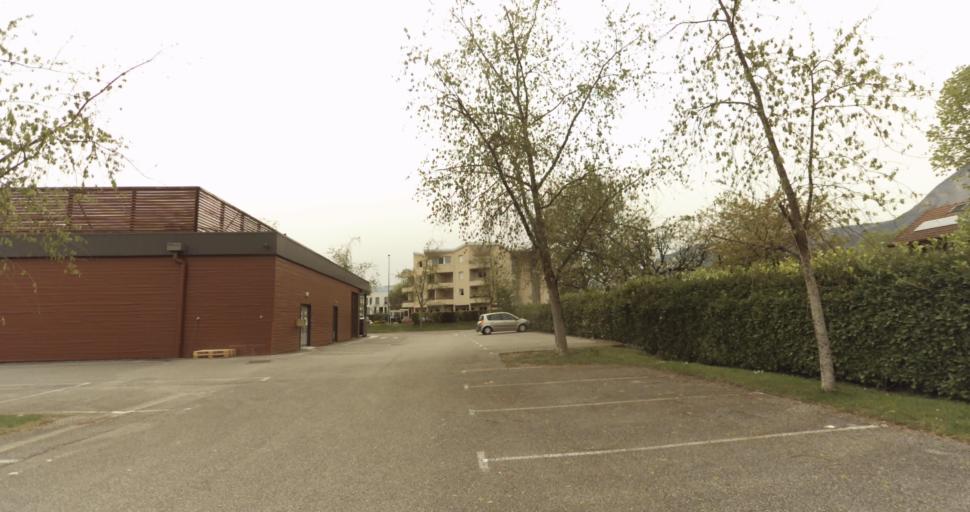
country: FR
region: Rhone-Alpes
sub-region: Departement de l'Isere
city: Montbonnot-Saint-Martin
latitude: 45.2180
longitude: 5.8094
